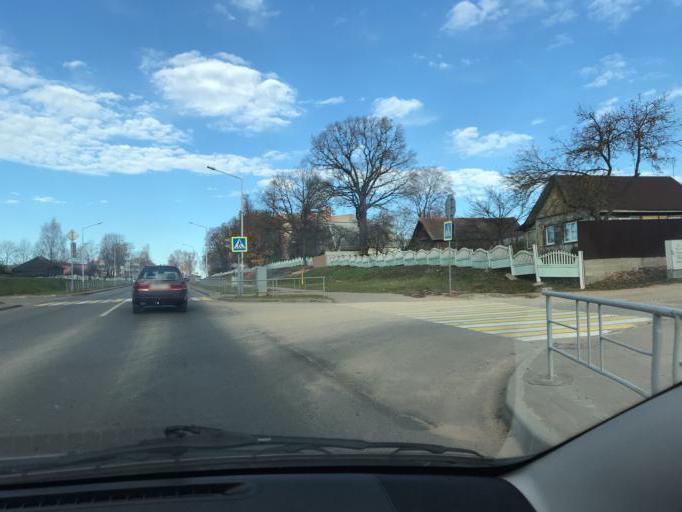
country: BY
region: Vitebsk
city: Haradok
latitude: 55.4692
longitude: 29.9730
